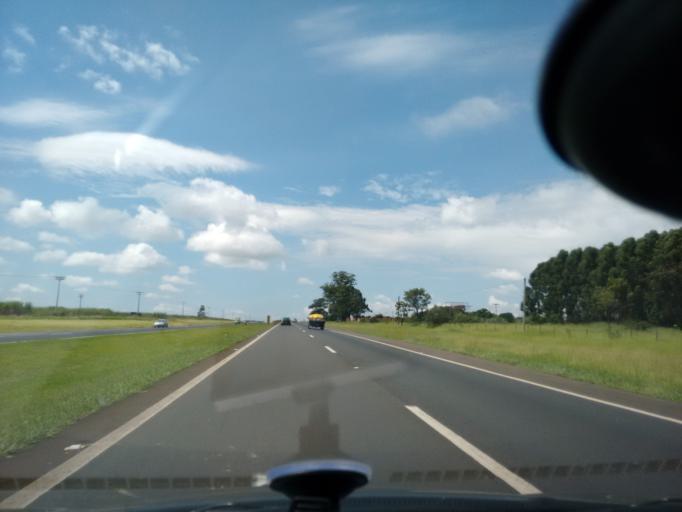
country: BR
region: Sao Paulo
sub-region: Ibate
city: Ibate
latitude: -21.9265
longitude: -48.0263
